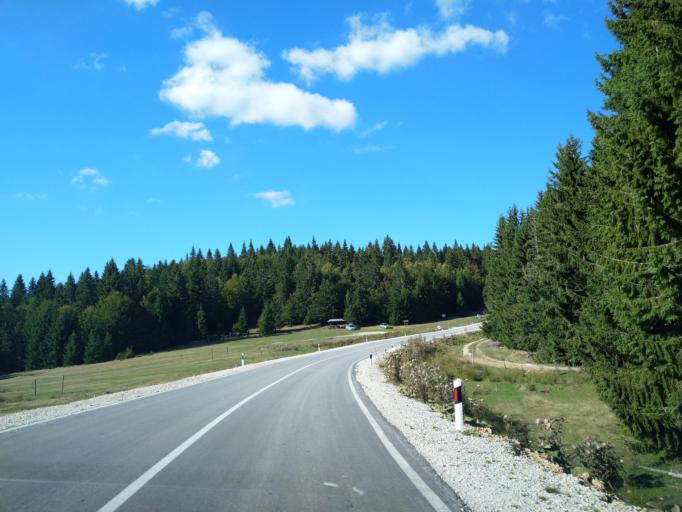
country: RS
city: Sokolovica
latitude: 43.2970
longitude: 20.3064
